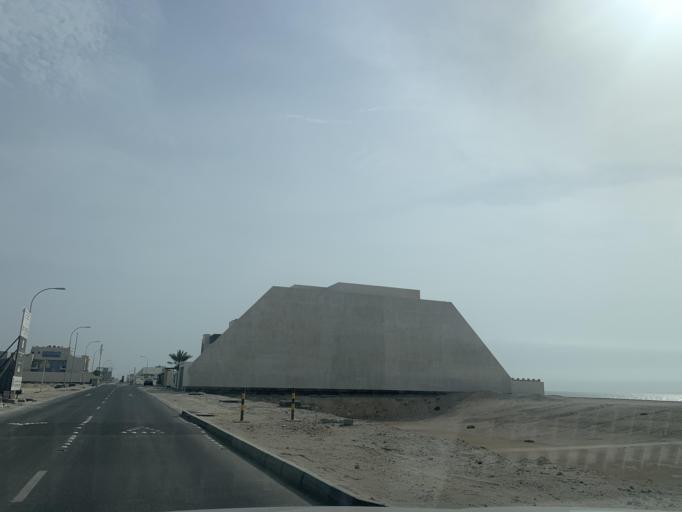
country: BH
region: Muharraq
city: Al Muharraq
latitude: 26.3227
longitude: 50.6242
